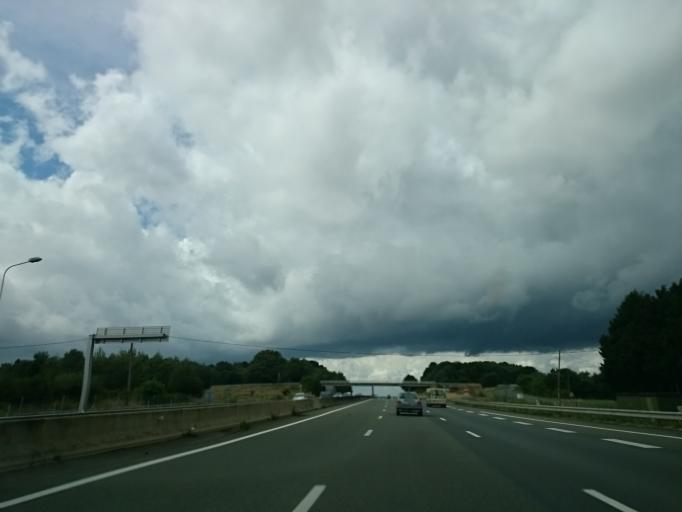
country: FR
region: Pays de la Loire
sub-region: Departement de la Sarthe
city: Sarge-les-le-Mans
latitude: 48.0566
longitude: 0.2491
